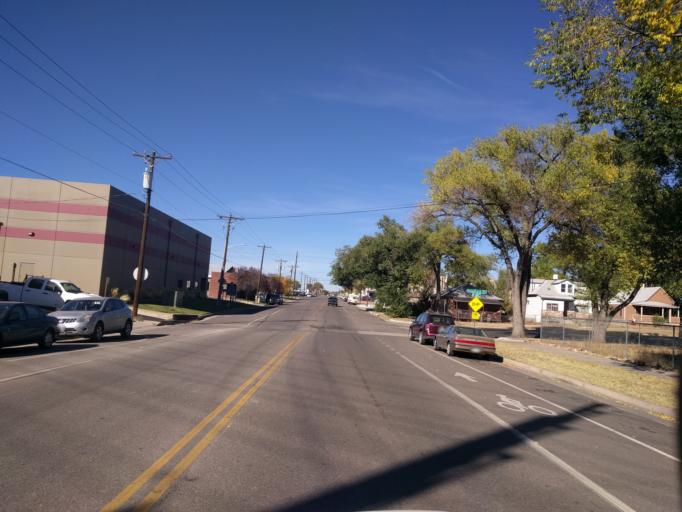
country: US
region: Colorado
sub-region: El Paso County
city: Colorado Springs
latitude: 38.8215
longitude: -104.8296
